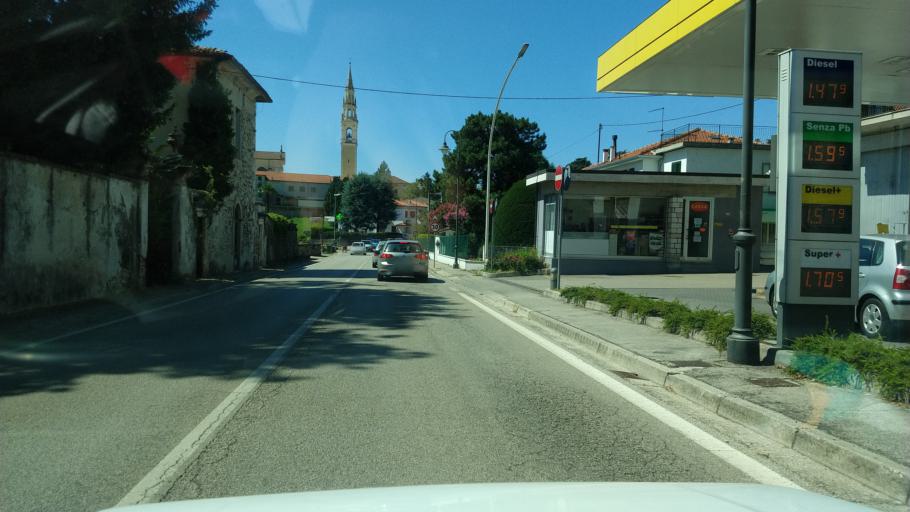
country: IT
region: Veneto
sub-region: Provincia di Vicenza
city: Mason Vicentino
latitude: 45.7201
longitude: 11.6092
